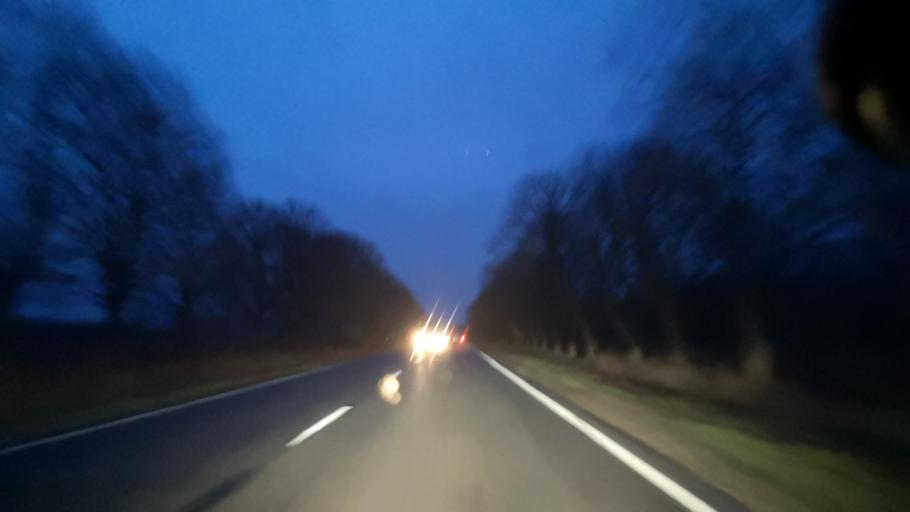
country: MD
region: Orhei
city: Orhei
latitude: 47.4777
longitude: 28.7915
